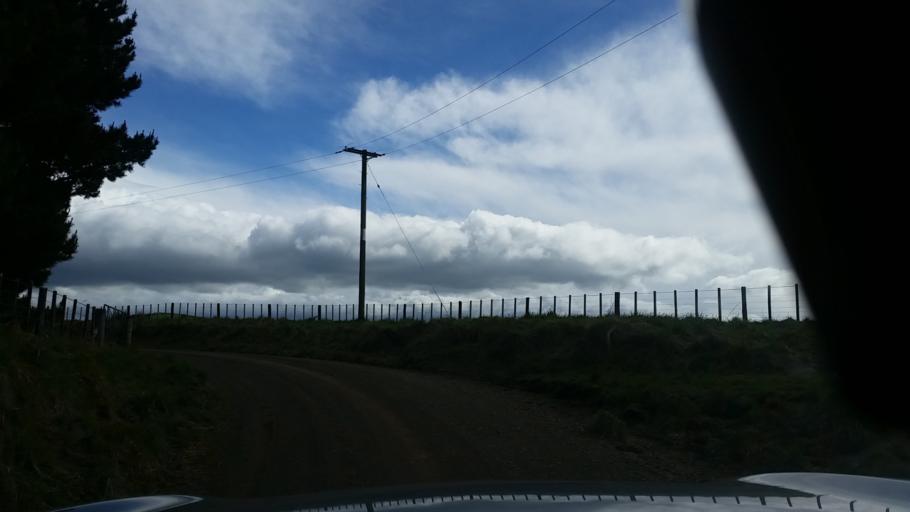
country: NZ
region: Hawke's Bay
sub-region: Napier City
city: Napier
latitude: -39.2158
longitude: 176.9825
